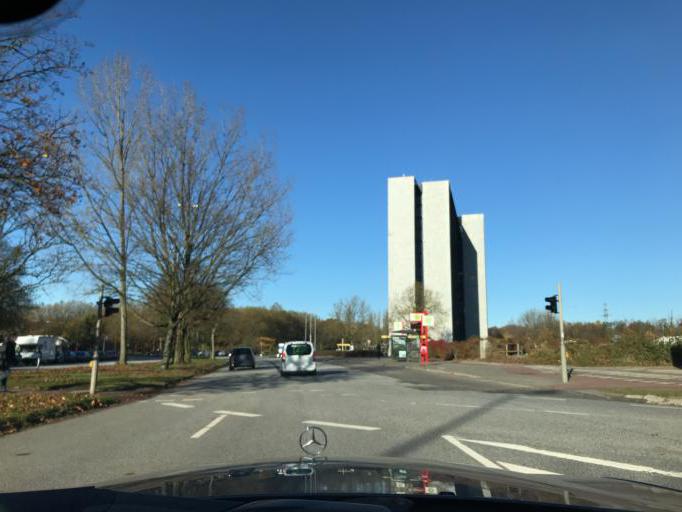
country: DE
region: Hamburg
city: Alsterdorf
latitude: 53.6055
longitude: 10.0253
